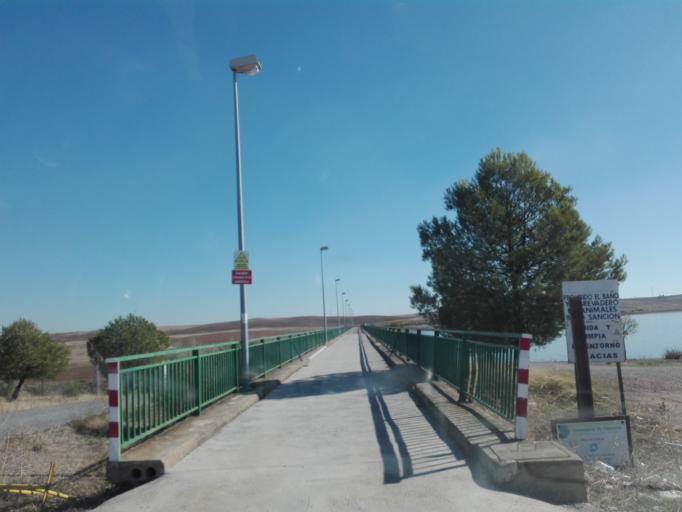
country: ES
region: Extremadura
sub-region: Provincia de Badajoz
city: Ahillones
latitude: 38.3135
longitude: -5.9146
